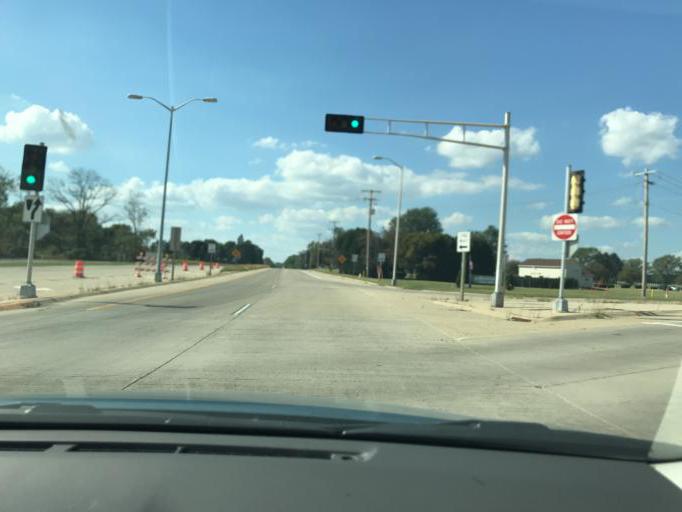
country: US
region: Wisconsin
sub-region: Walworth County
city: Williams Bay
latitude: 42.6002
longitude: -88.5408
